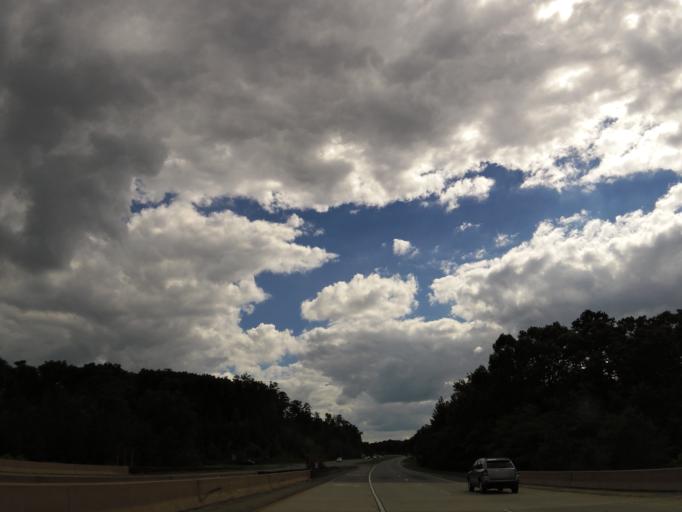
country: US
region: Georgia
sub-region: Walker County
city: Fairview
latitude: 34.9435
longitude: -85.2778
